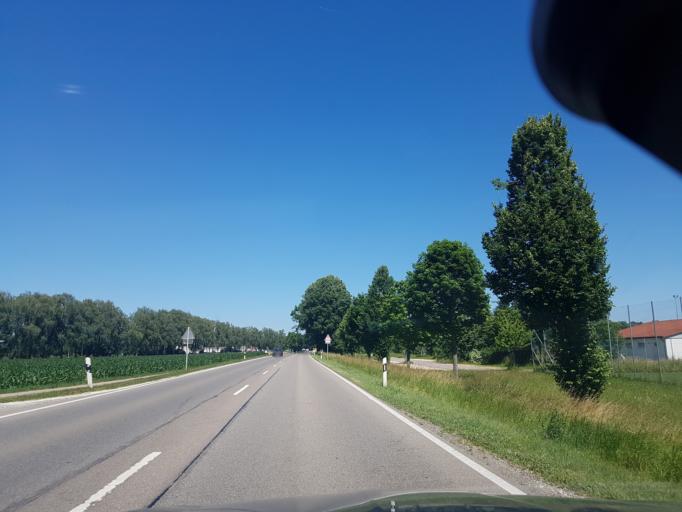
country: DE
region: Bavaria
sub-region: Swabia
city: Weissenhorn
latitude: 48.2987
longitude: 10.1475
